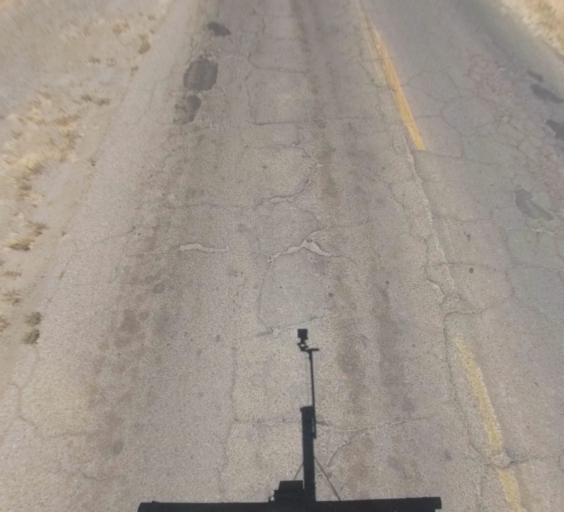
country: US
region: California
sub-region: Madera County
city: Parksdale
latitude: 36.9475
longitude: -120.0285
